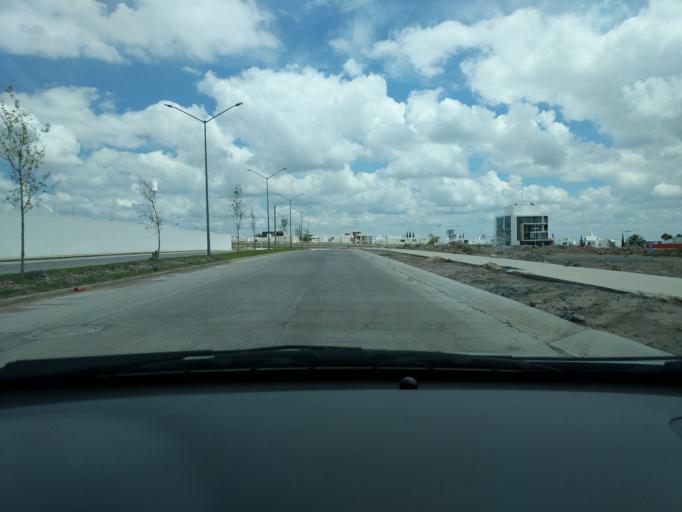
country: MX
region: San Luis Potosi
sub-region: Mexquitic de Carmona
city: Guadalupe Victoria
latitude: 22.1662
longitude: -101.0458
